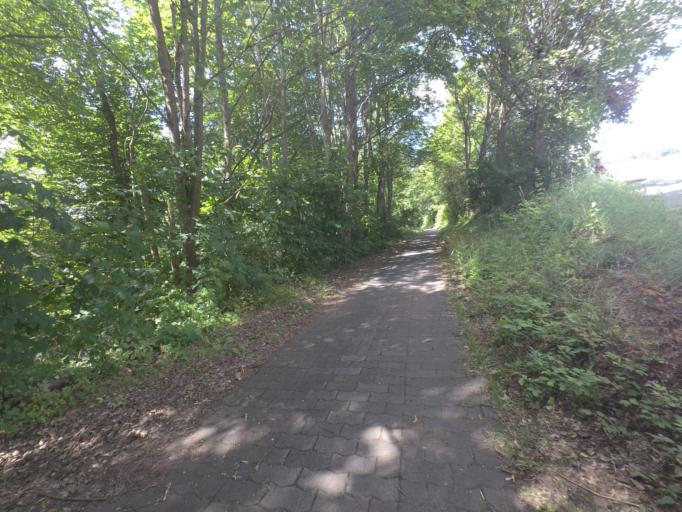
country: DE
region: Rheinland-Pfalz
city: Gerolstein
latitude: 50.2222
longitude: 6.6444
